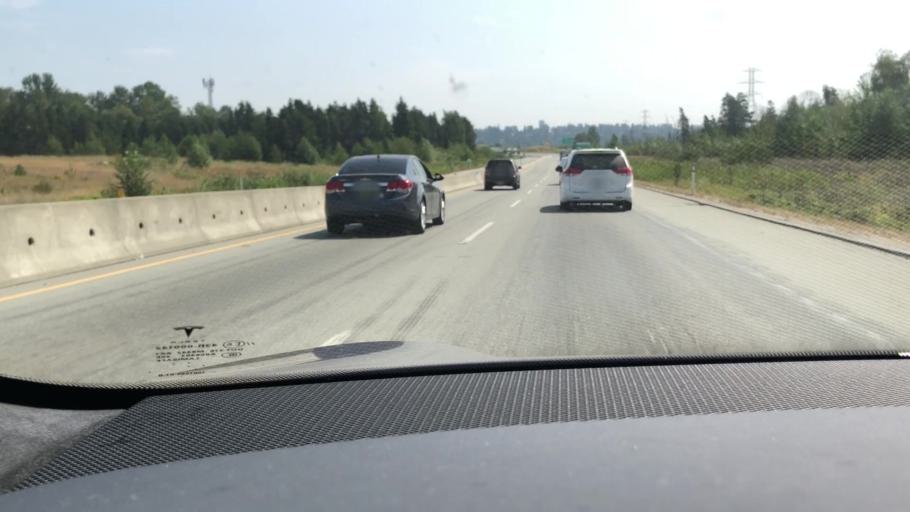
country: CA
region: British Columbia
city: Delta
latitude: 49.1484
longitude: -122.9630
